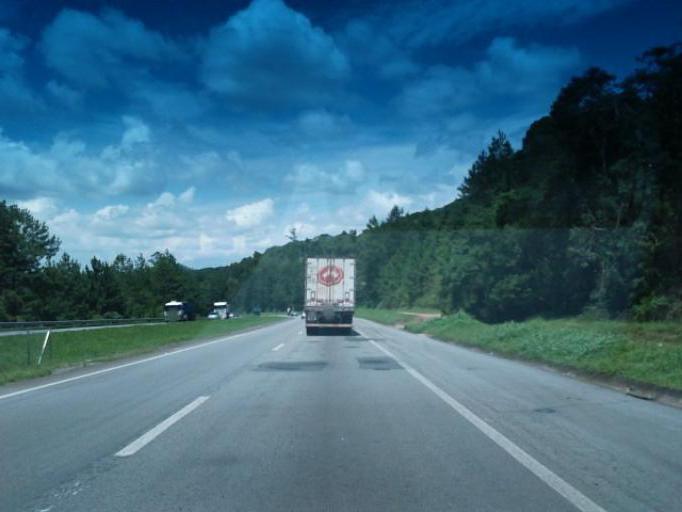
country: BR
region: Sao Paulo
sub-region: Juquitiba
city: Juquitiba
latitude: -23.9381
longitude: -47.0840
